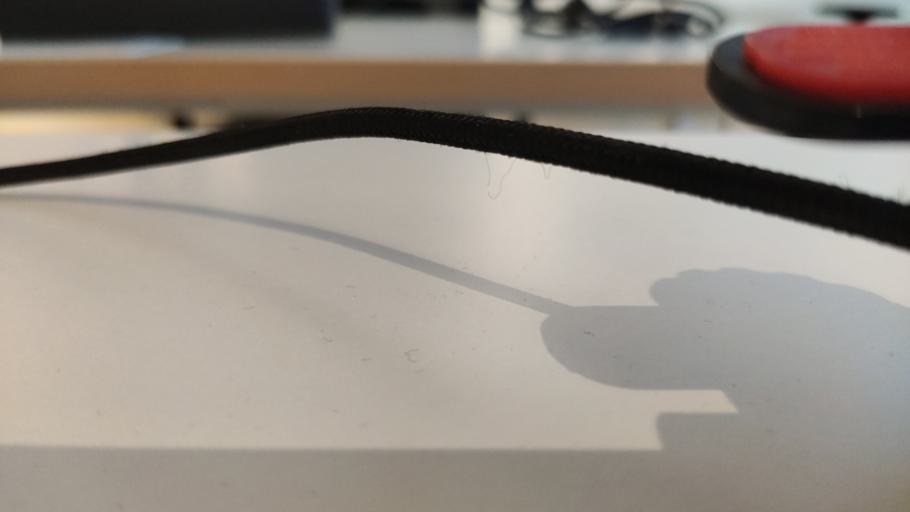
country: RU
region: Moskovskaya
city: Novopetrovskoye
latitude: 55.8746
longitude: 36.4050
